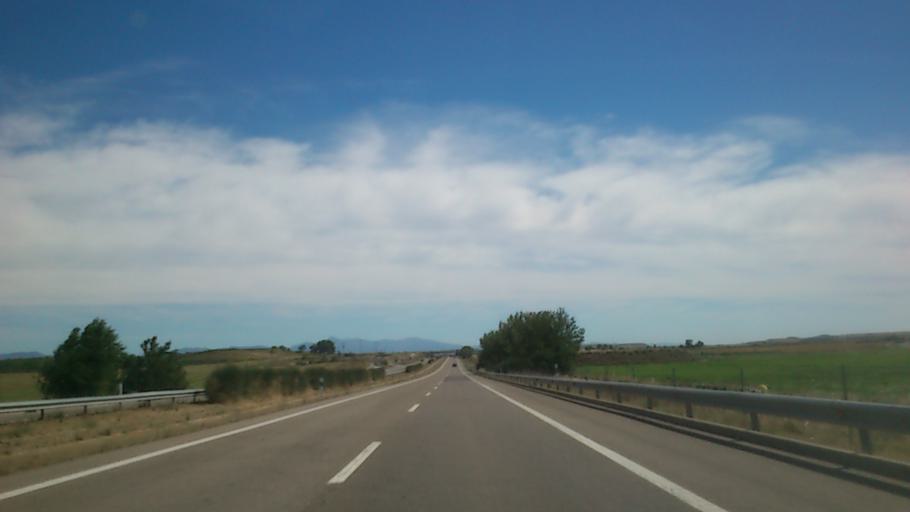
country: ES
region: Aragon
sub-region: Provincia de Huesca
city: Almudebar
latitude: 42.0158
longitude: -0.6178
